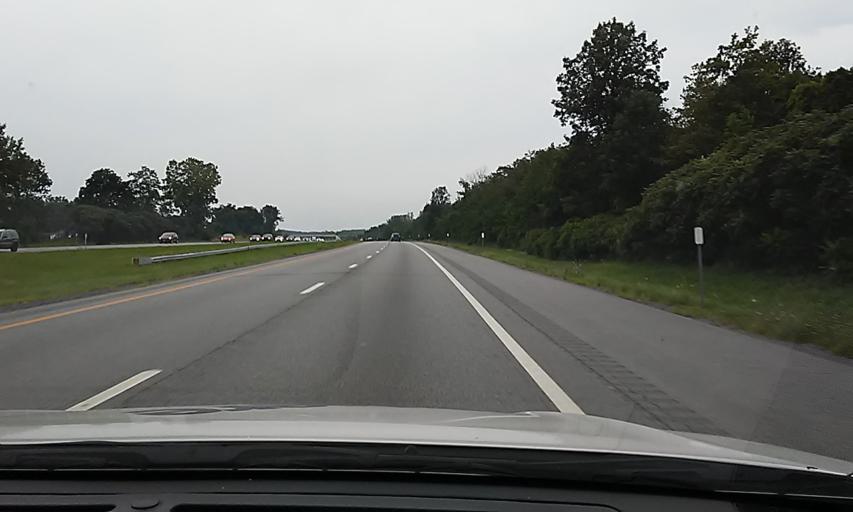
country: US
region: New York
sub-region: Erie County
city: Akron
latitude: 42.9787
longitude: -78.5037
